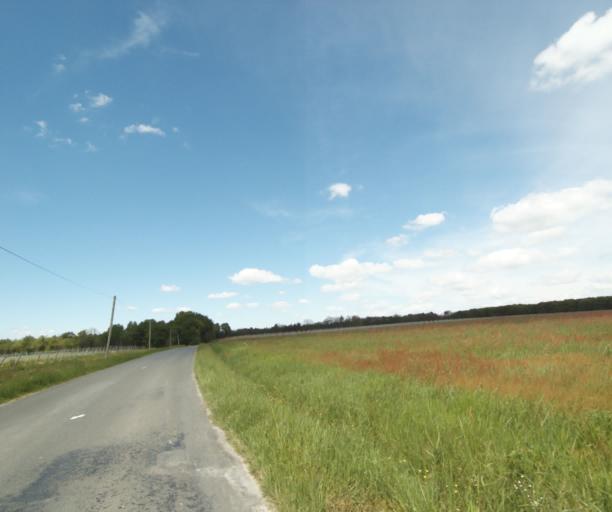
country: FR
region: Poitou-Charentes
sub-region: Departement de la Charente-Maritime
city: Burie
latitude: 45.7546
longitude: -0.4618
